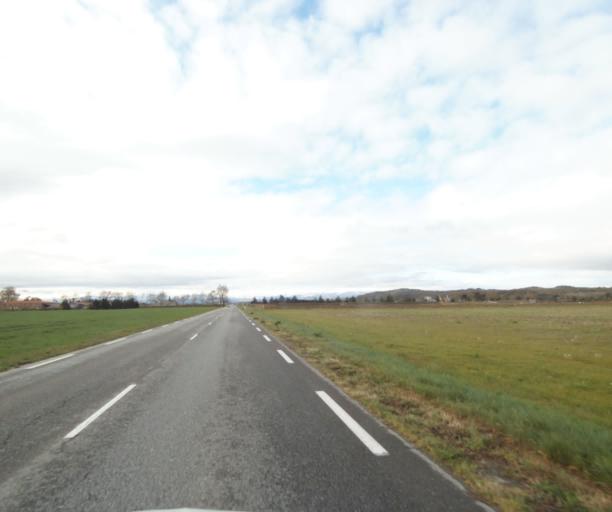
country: FR
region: Midi-Pyrenees
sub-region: Departement de l'Ariege
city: Saverdun
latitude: 43.2168
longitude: 1.6074
